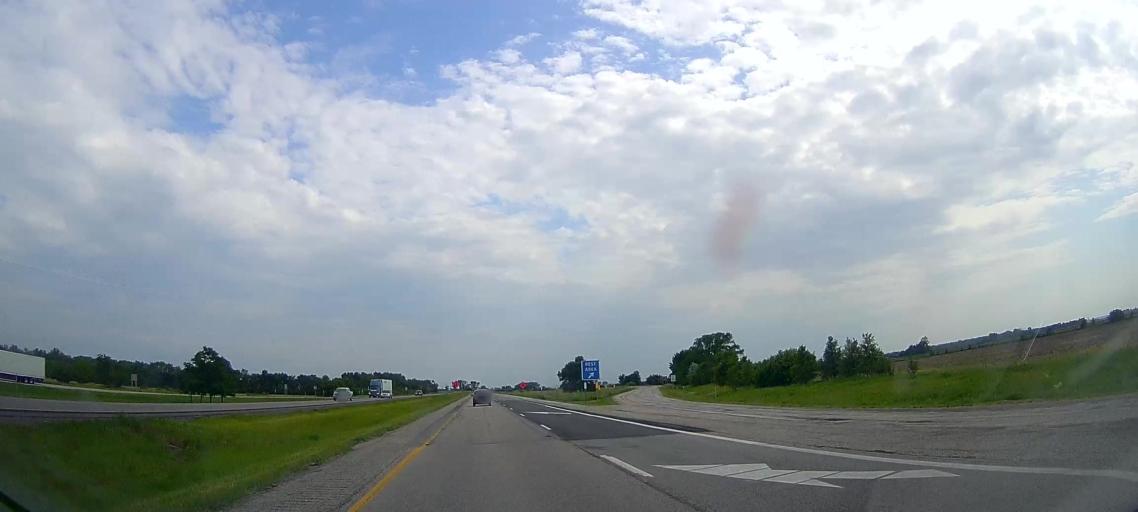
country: US
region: Nebraska
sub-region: Burt County
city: Tekamah
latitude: 41.7440
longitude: -96.0476
